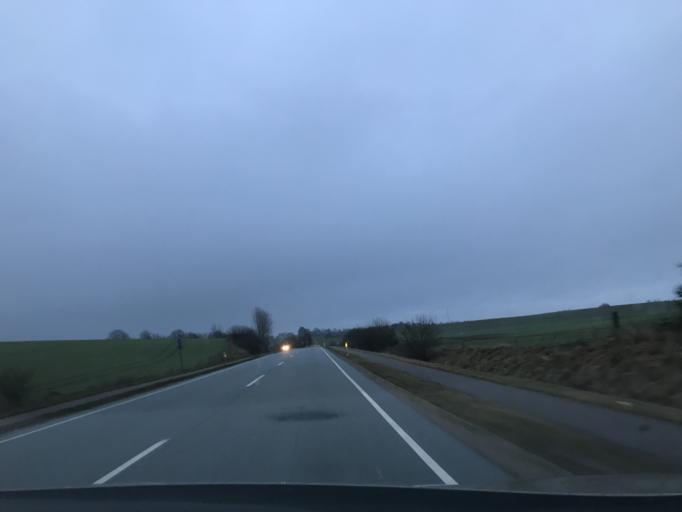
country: DK
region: Central Jutland
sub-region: Hedensted Kommune
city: Hedensted
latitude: 55.7056
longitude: 9.7611
